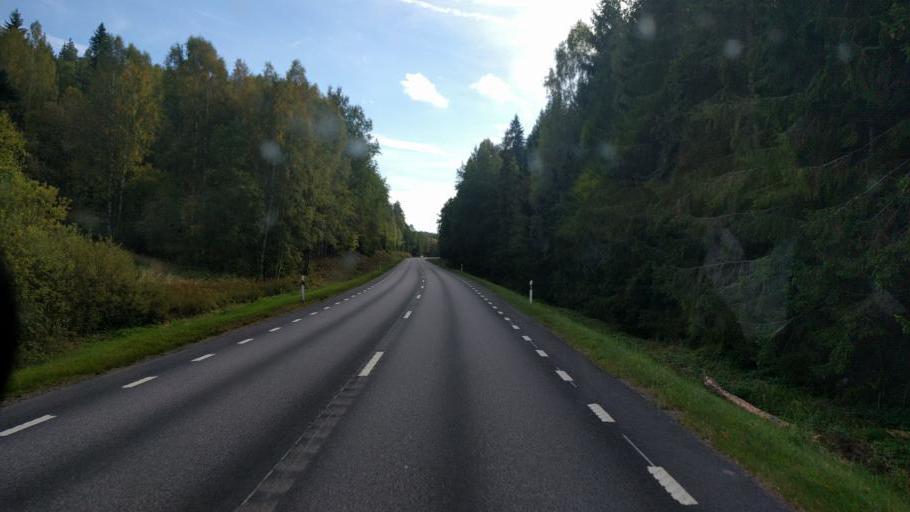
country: SE
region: OEstergoetland
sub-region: Kinda Kommun
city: Kisa
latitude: 57.9538
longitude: 15.6614
